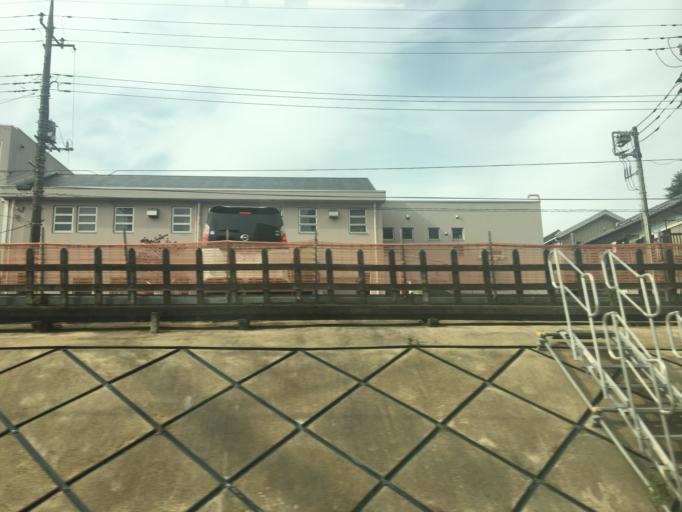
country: JP
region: Saitama
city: Sayama
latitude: 35.8493
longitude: 139.4155
